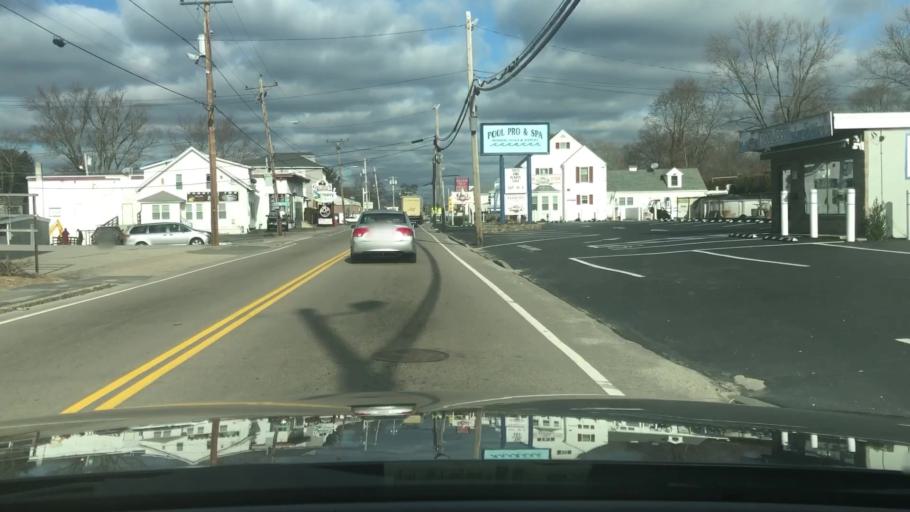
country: US
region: Rhode Island
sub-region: Providence County
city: Woonsocket
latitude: 42.0202
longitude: -71.4948
